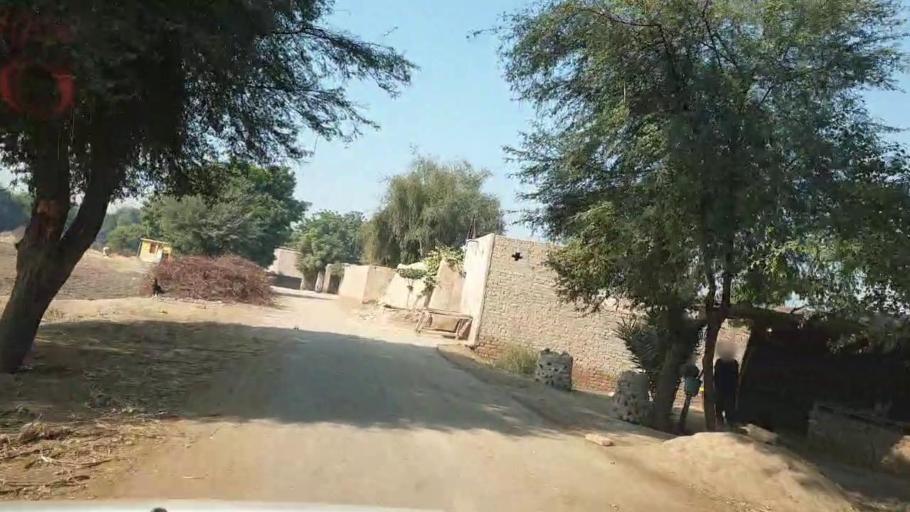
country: PK
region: Sindh
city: Bhan
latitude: 26.6040
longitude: 67.7484
